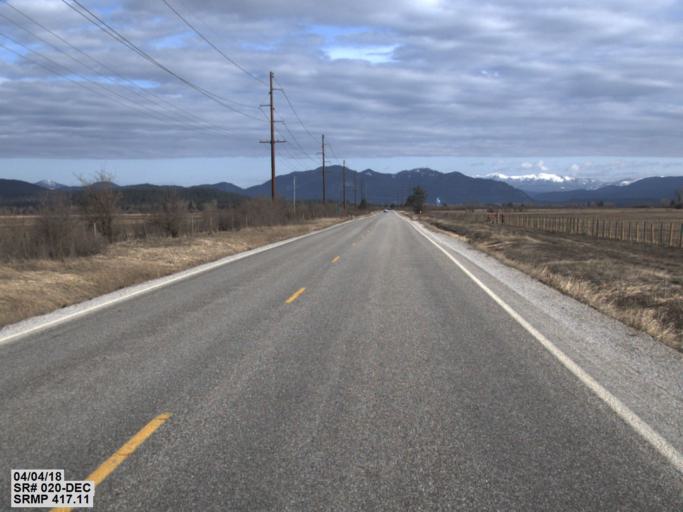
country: US
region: Washington
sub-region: Pend Oreille County
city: Newport
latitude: 48.3652
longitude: -117.3047
